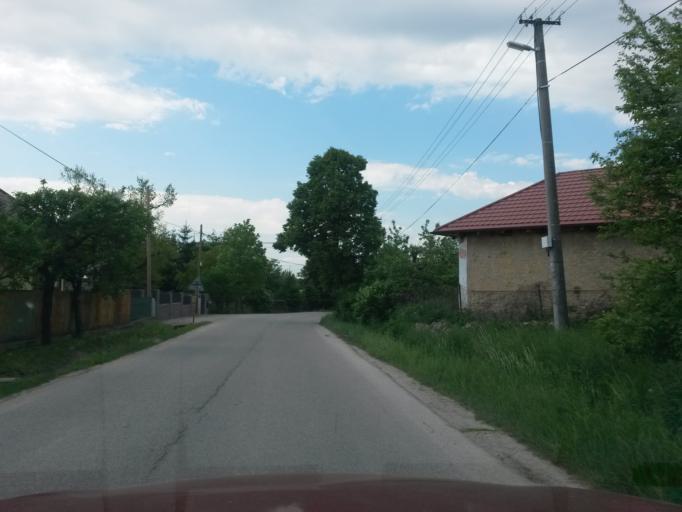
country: SK
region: Kosicky
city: Moldava nad Bodvou
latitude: 48.6933
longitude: 21.0102
